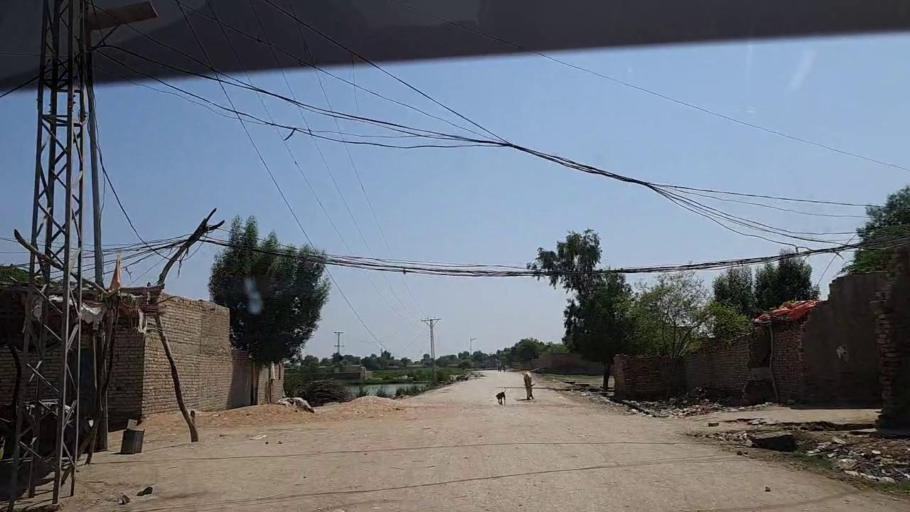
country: PK
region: Sindh
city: Ghauspur
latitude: 28.1428
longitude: 69.0878
